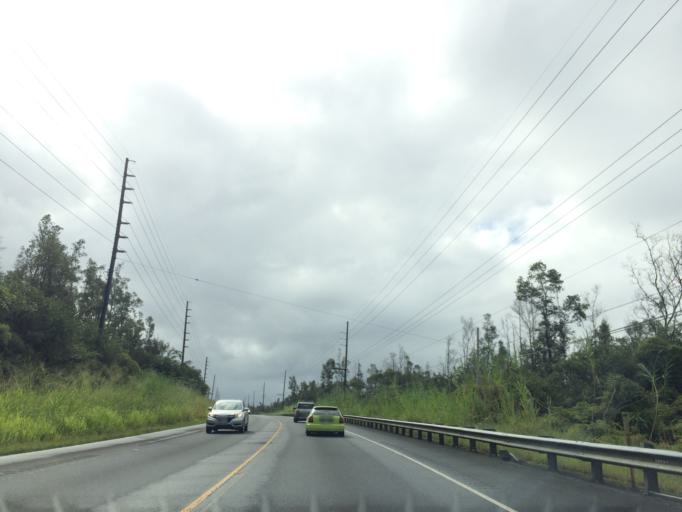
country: US
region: Hawaii
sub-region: Hawaii County
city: Hawaiian Paradise Park
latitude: 19.5236
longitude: -154.9692
